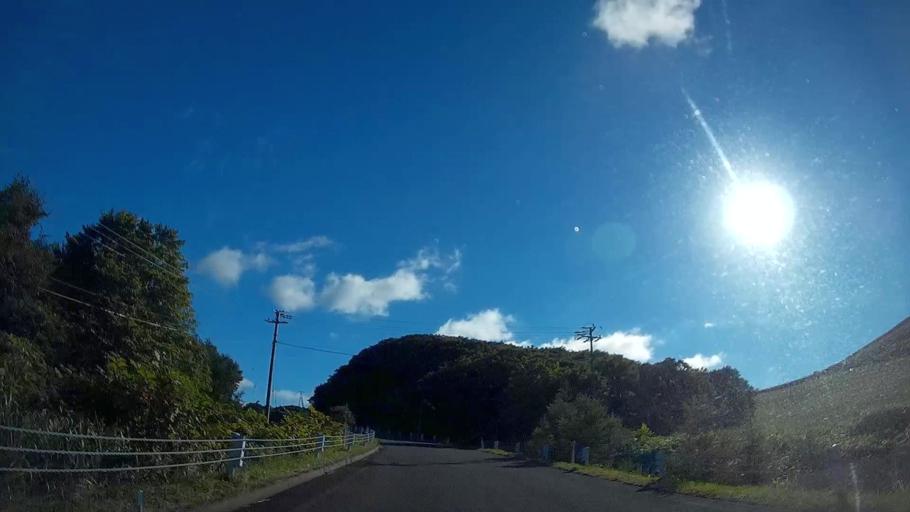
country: JP
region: Hokkaido
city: Iwanai
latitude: 42.4596
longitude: 139.8585
